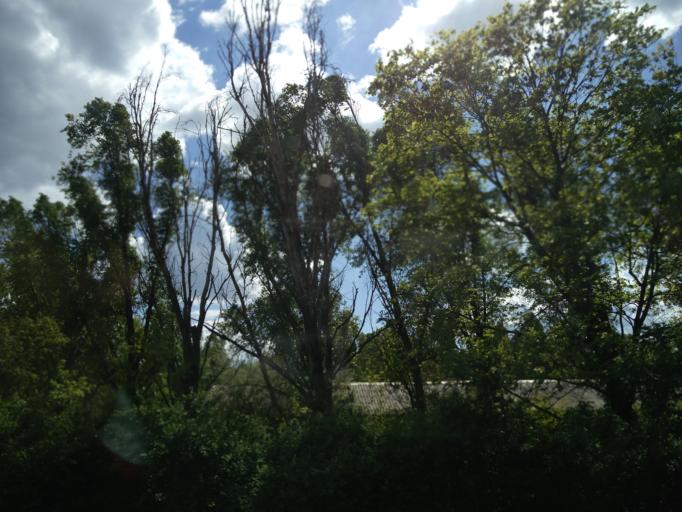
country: HU
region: Pest
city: Vecses
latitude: 47.4208
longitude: 19.2534
